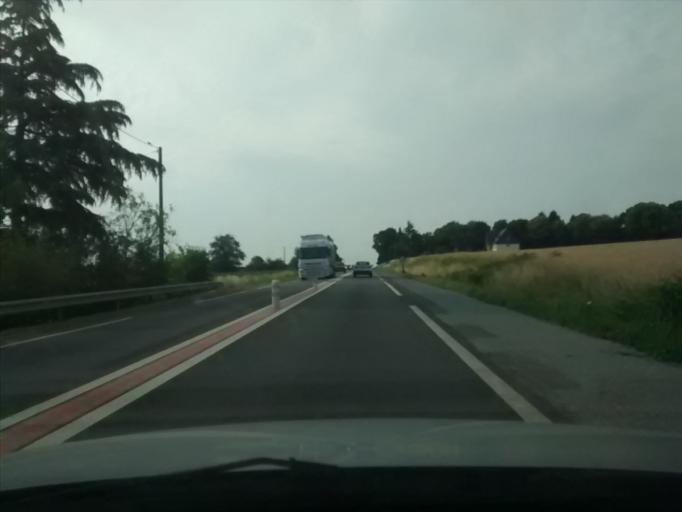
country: FR
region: Brittany
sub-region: Departement d'Ille-et-Vilaine
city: Etrelles
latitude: 48.0841
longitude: -1.2024
